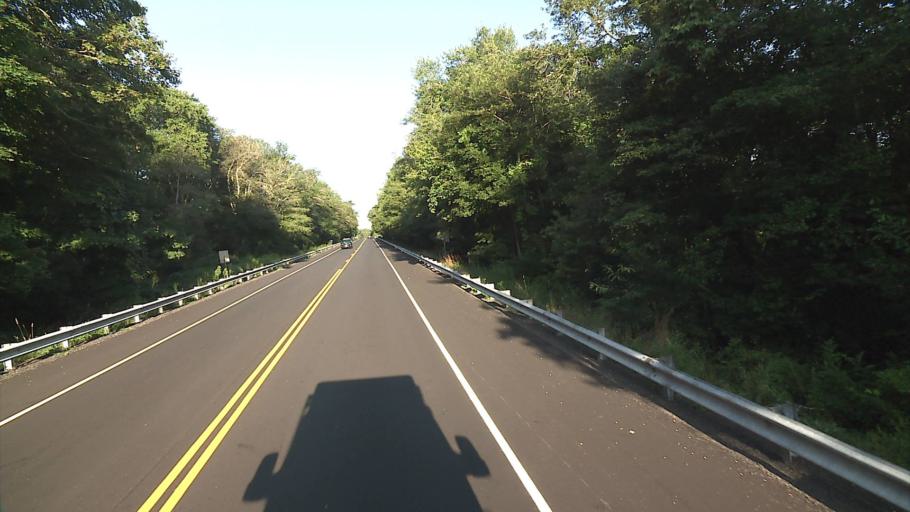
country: US
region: Connecticut
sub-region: New London County
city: Mystic
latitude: 41.3506
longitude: -71.8989
